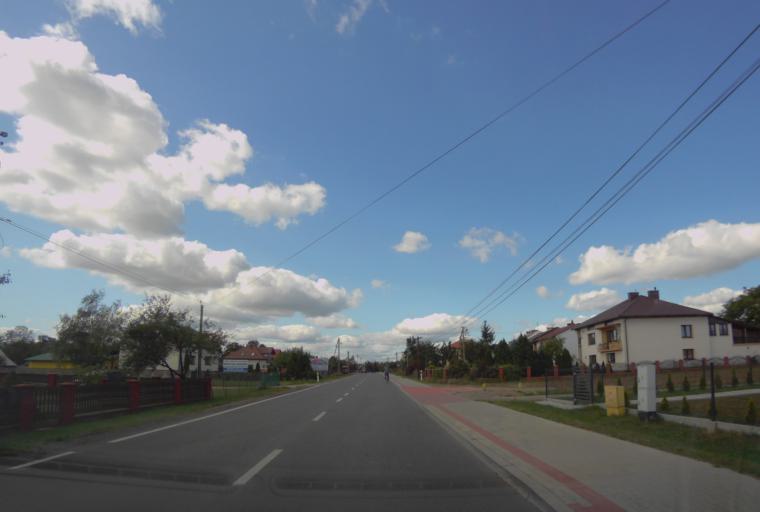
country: PL
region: Subcarpathian Voivodeship
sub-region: Powiat nizanski
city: Jezowe
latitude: 50.3684
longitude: 22.1754
